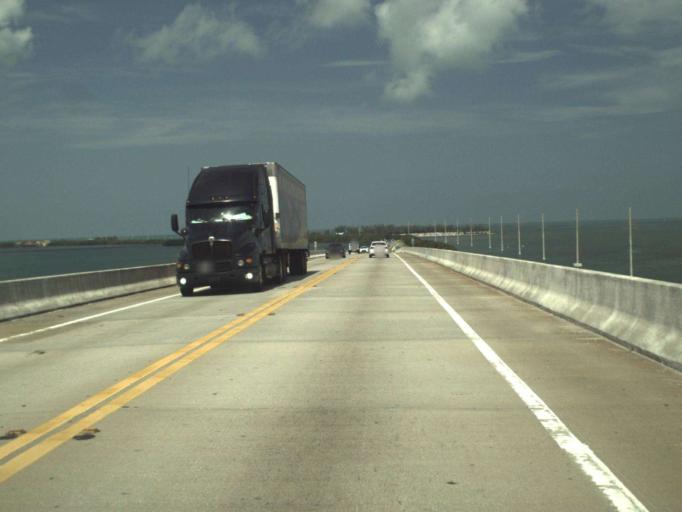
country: US
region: Florida
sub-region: Monroe County
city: Islamorada
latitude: 24.8385
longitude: -80.7756
